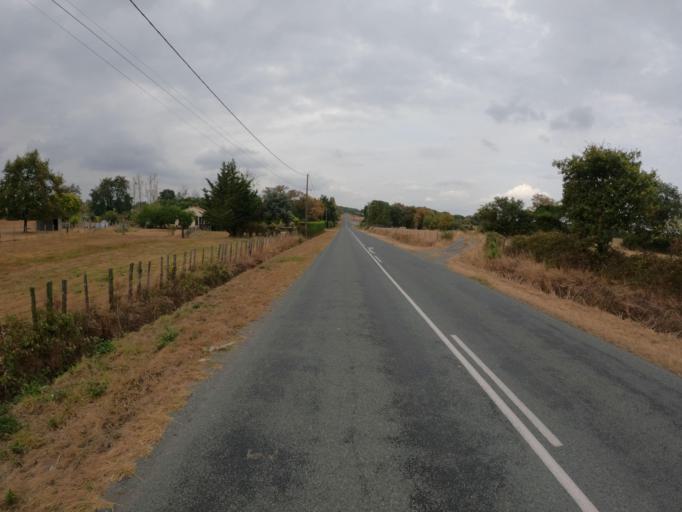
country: FR
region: Pays de la Loire
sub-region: Departement de Maine-et-Loire
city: Le Longeron
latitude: 47.0256
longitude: -1.0506
